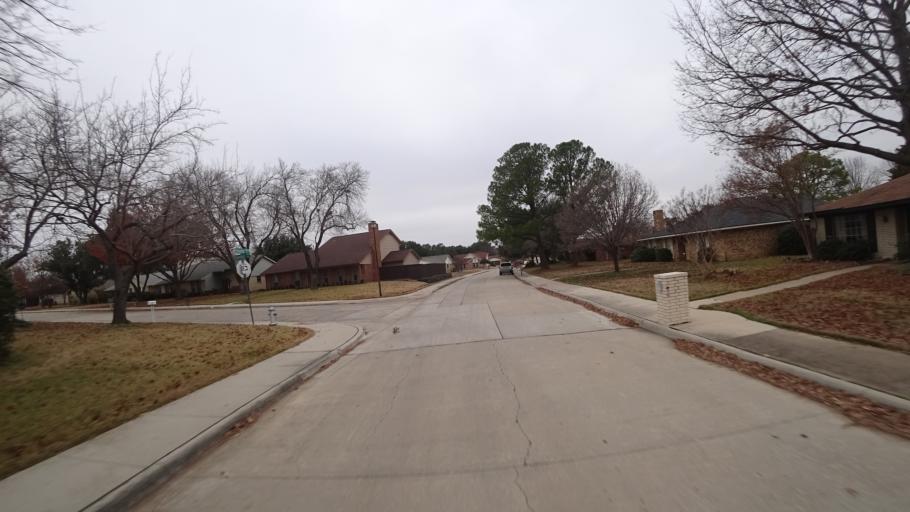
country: US
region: Texas
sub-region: Denton County
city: Highland Village
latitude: 33.0510
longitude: -97.0378
